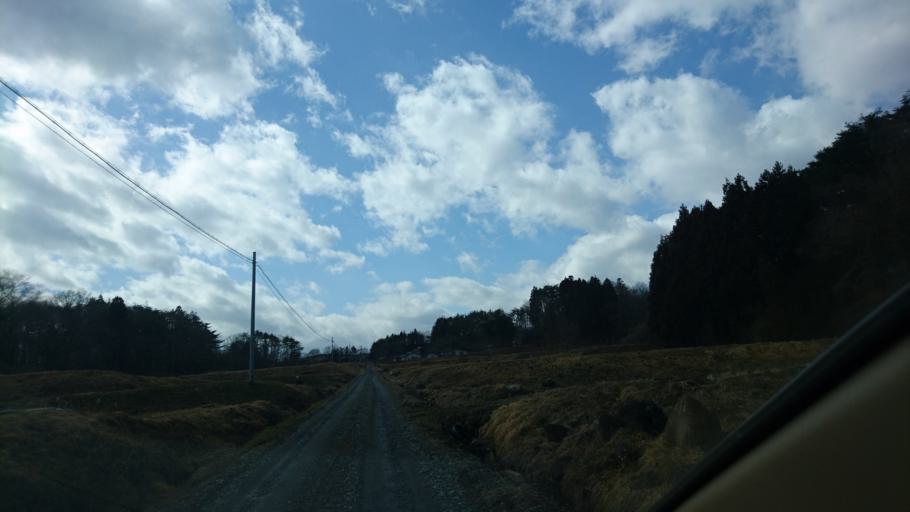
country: JP
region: Iwate
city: Ichinoseki
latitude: 38.9539
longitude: 141.1120
